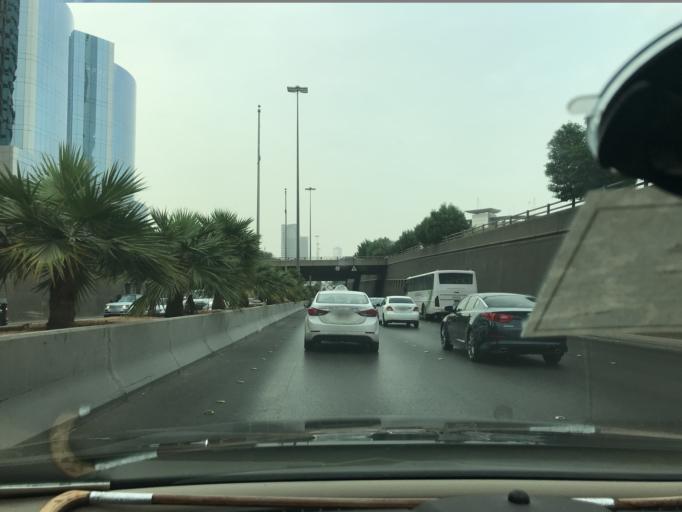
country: SA
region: Ar Riyad
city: Riyadh
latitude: 24.7103
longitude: 46.6726
